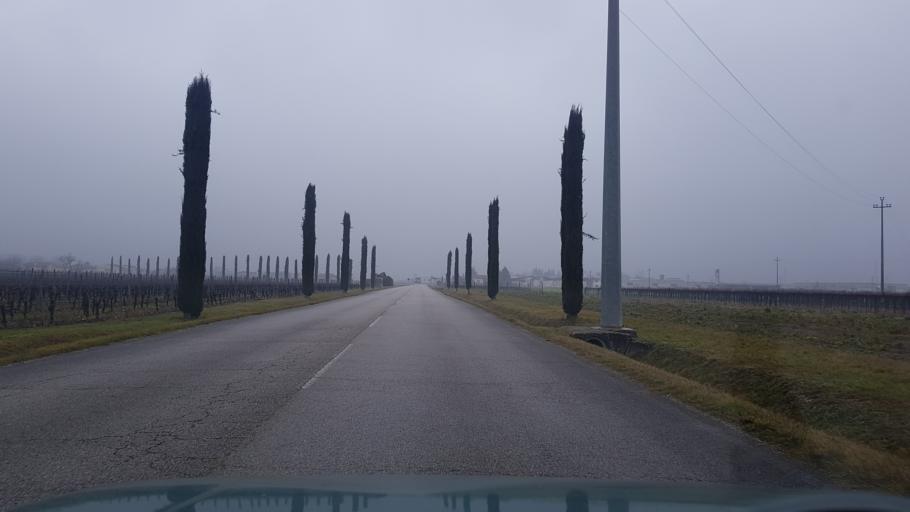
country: IT
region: Friuli Venezia Giulia
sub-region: Provincia di Udine
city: Chiopris
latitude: 45.9239
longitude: 13.3908
